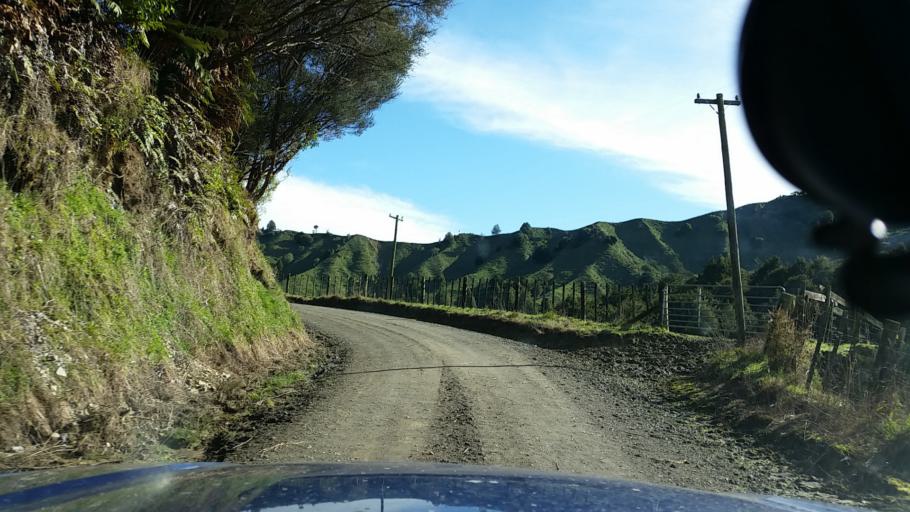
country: NZ
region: Taranaki
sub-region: New Plymouth District
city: Waitara
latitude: -39.0511
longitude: 174.7602
